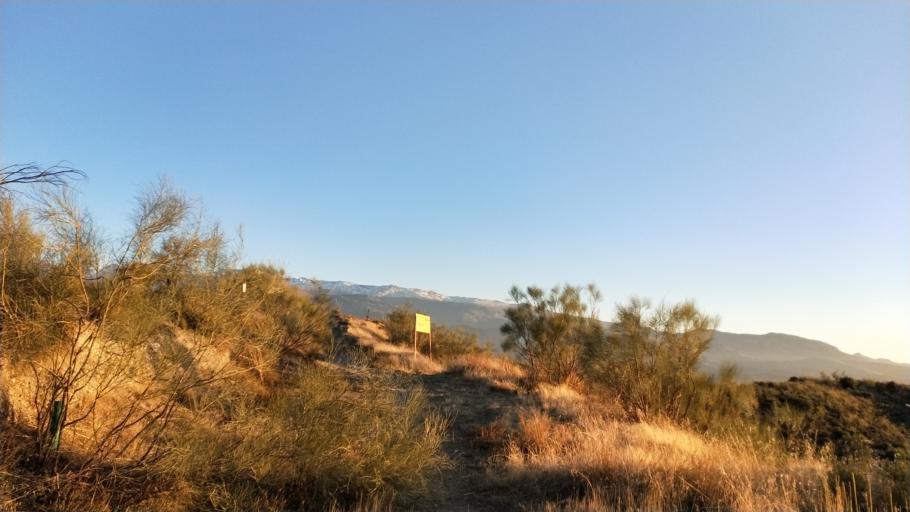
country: ES
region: Andalusia
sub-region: Provincia de Granada
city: Beas de Granada
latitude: 37.2064
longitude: -3.4977
